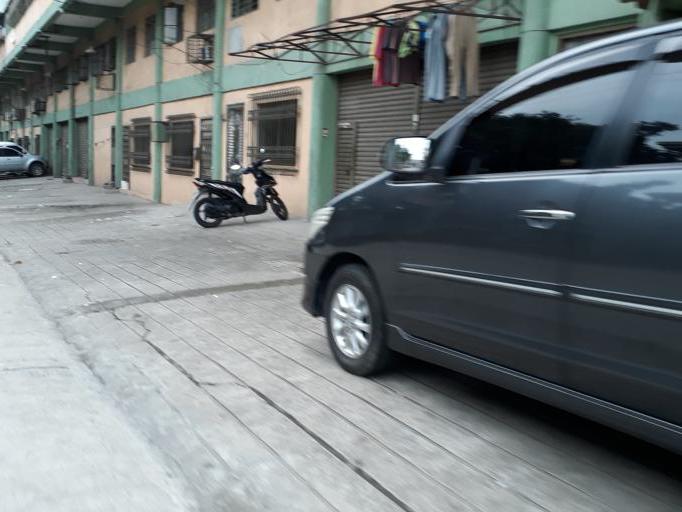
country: PH
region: Calabarzon
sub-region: Province of Rizal
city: Valenzuela
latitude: 14.6807
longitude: 120.9772
